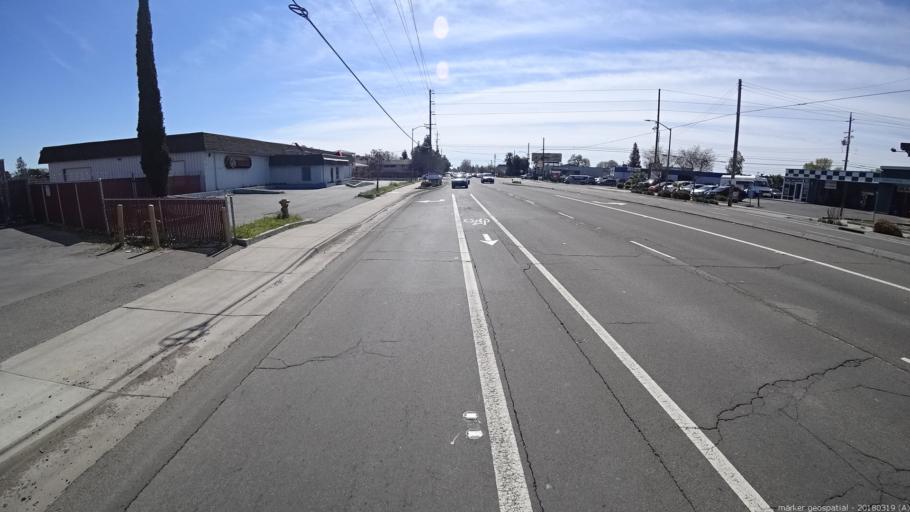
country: US
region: California
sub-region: Sacramento County
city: Parkway
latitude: 38.5056
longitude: -121.4643
